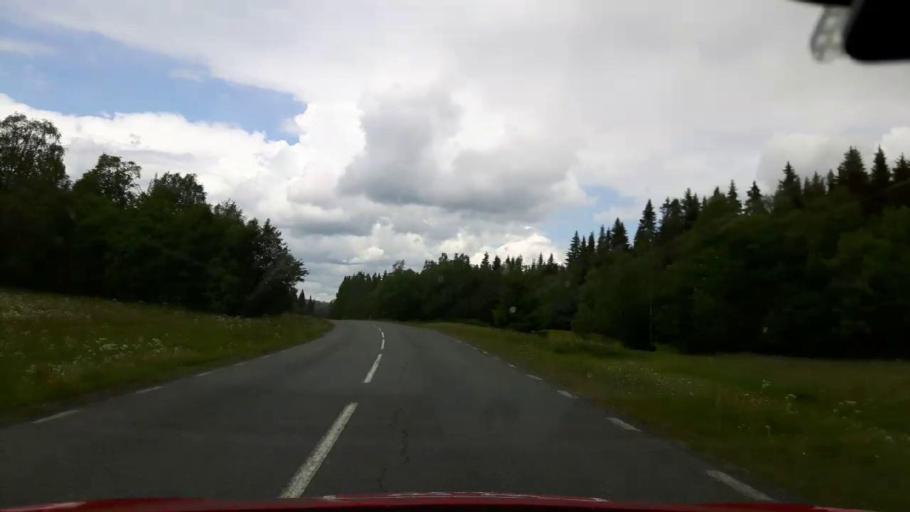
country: SE
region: Jaemtland
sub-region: Krokoms Kommun
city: Krokom
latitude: 63.4959
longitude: 14.2138
